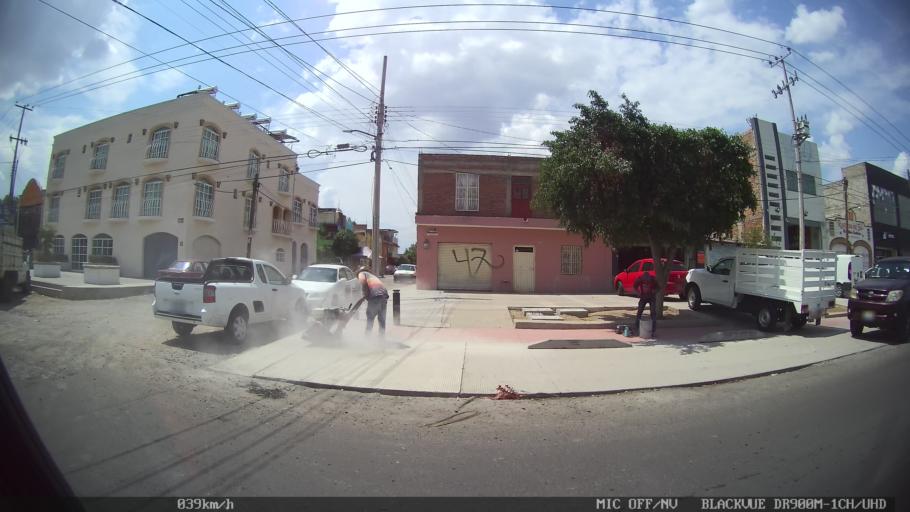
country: MX
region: Jalisco
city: Tonala
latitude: 20.6182
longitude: -103.2577
